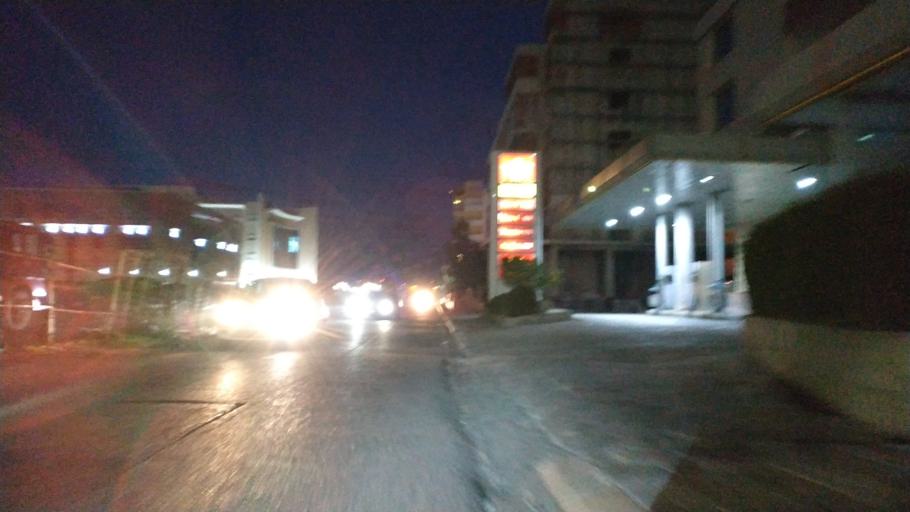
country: AL
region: Shkoder
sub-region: Rrethi i Shkodres
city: Shkoder
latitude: 42.0550
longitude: 19.4989
